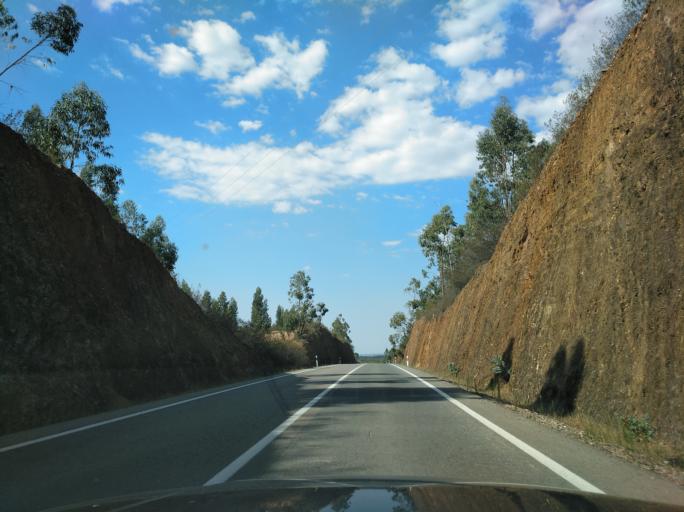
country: ES
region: Andalusia
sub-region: Provincia de Huelva
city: Santa Barbara de Casa
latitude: 37.8336
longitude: -7.2061
